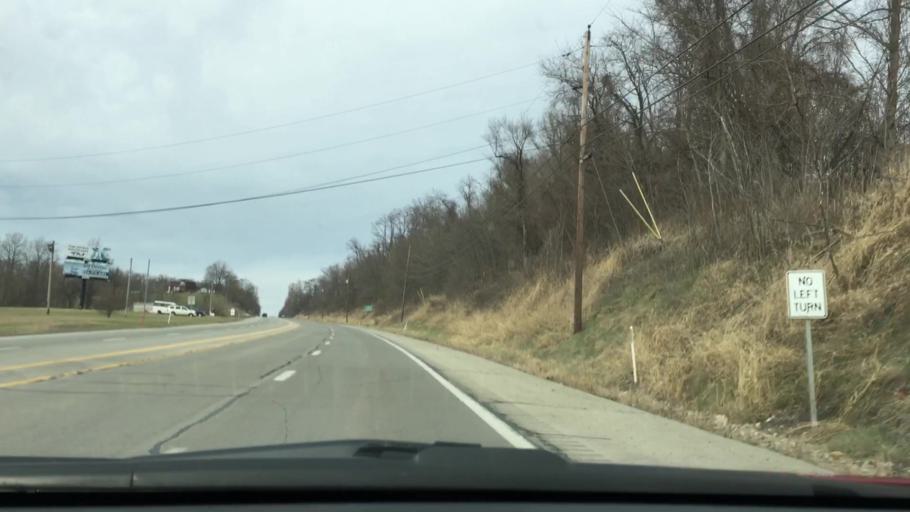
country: US
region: Pennsylvania
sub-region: Fayette County
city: Perryopolis
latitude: 40.0973
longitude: -79.7632
